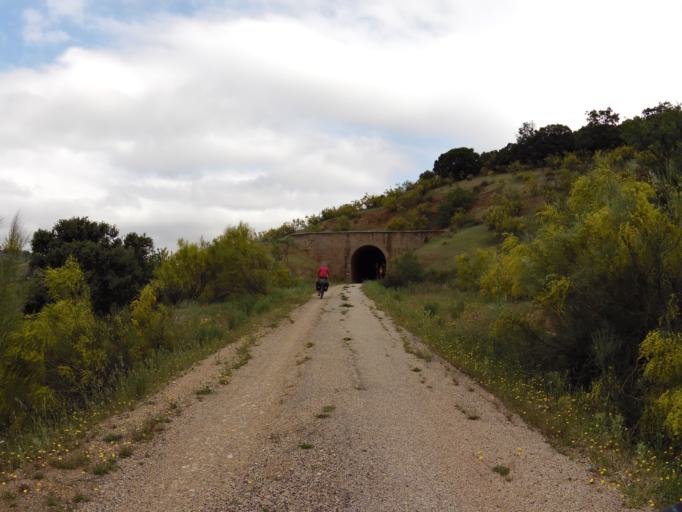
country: ES
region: Castille-La Mancha
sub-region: Provincia de Albacete
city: Alcaraz
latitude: 38.7036
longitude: -2.5017
